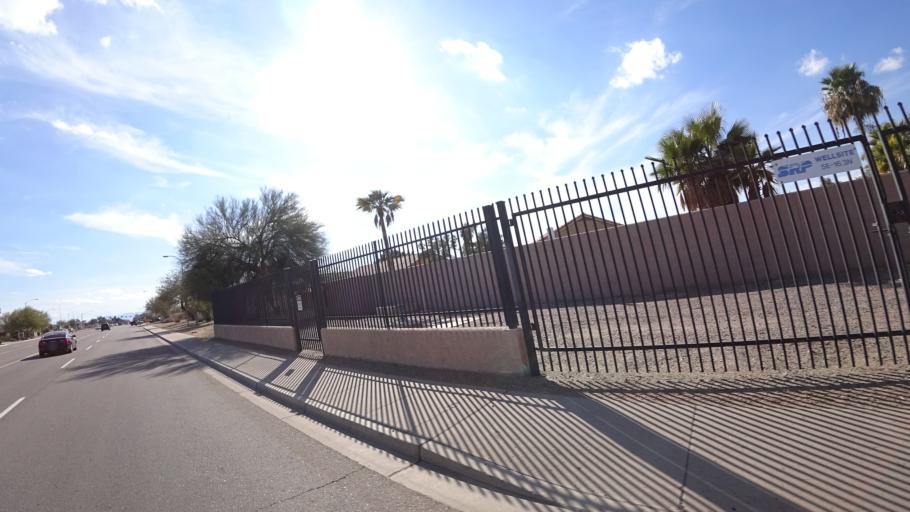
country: US
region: Arizona
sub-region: Maricopa County
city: Peoria
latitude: 33.6136
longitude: -112.2201
